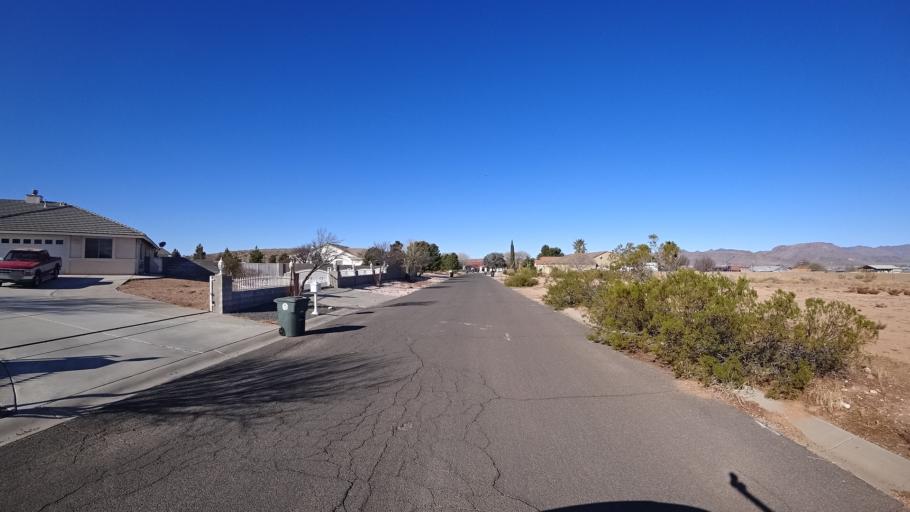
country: US
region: Arizona
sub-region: Mohave County
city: Kingman
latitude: 35.2084
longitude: -113.9988
